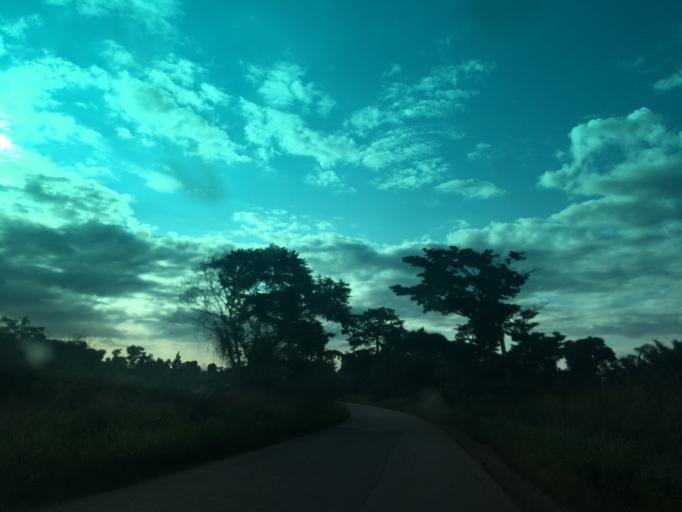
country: GH
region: Western
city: Bibiani
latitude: 6.2953
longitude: -2.2371
